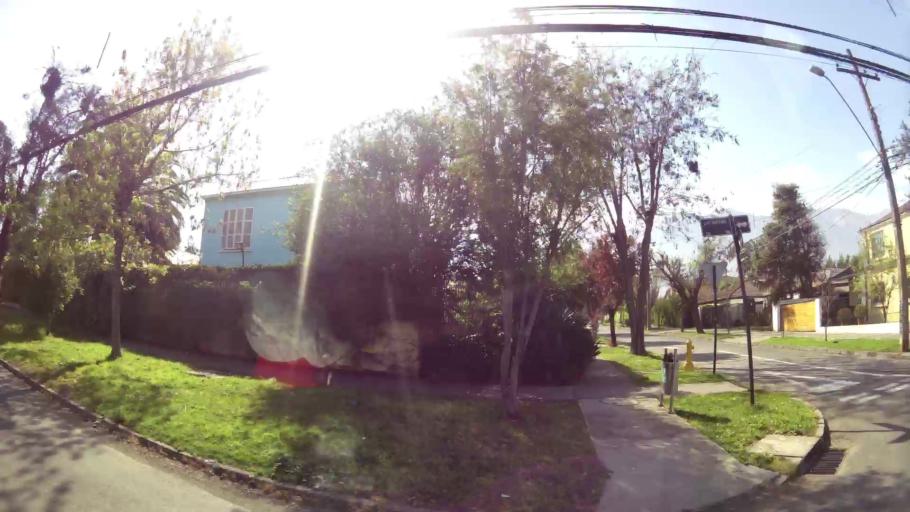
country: CL
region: Santiago Metropolitan
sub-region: Provincia de Santiago
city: Villa Presidente Frei, Nunoa, Santiago, Chile
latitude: -33.4548
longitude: -70.5549
